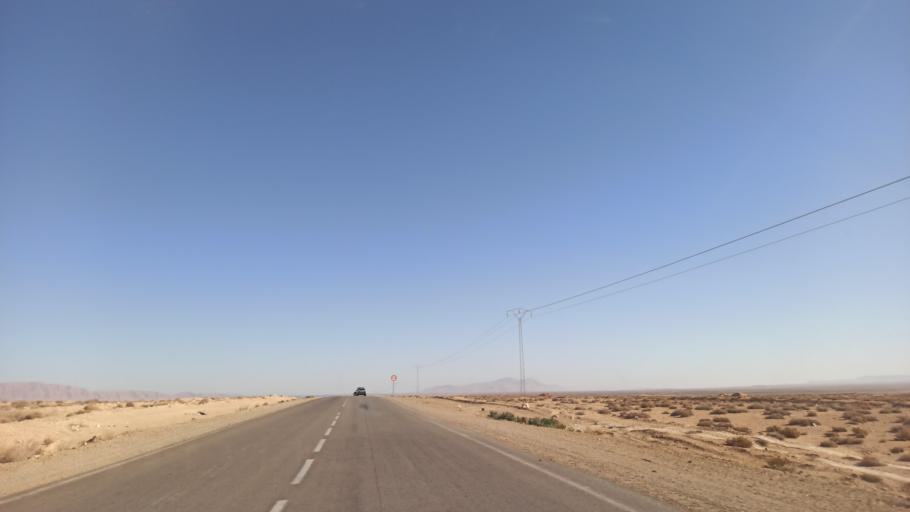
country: TN
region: Gafsa
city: Al Metlaoui
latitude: 34.3265
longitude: 8.5399
